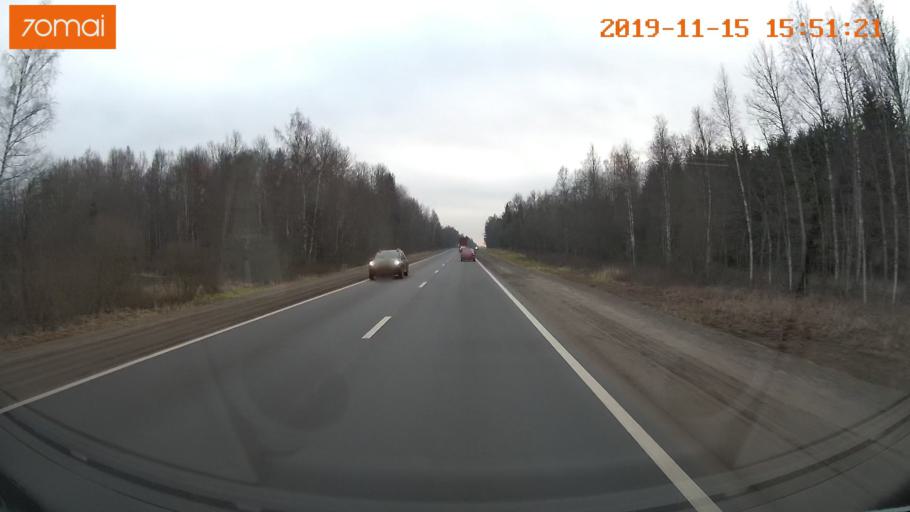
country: RU
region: Jaroslavl
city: Yaroslavl
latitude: 57.8955
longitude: 40.0082
